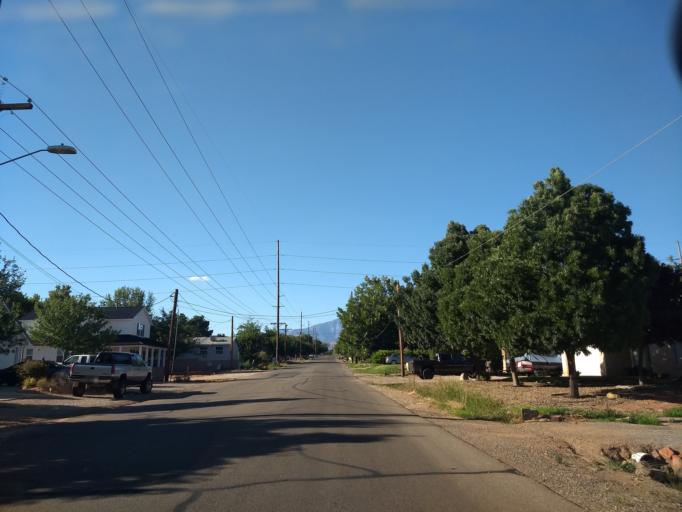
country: US
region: Utah
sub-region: Washington County
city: Washington
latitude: 37.1240
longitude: -113.5082
